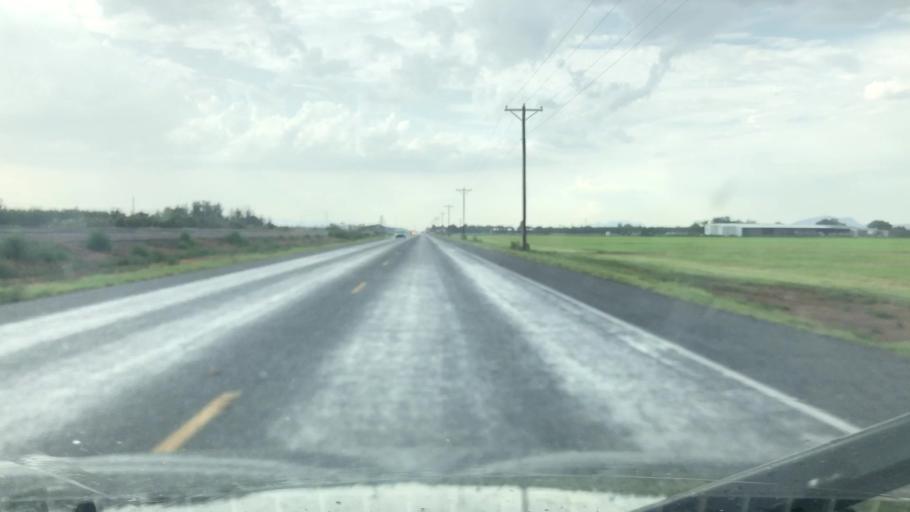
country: US
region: New Mexico
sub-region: Dona Ana County
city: Mesquite
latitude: 32.1534
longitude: -106.6895
